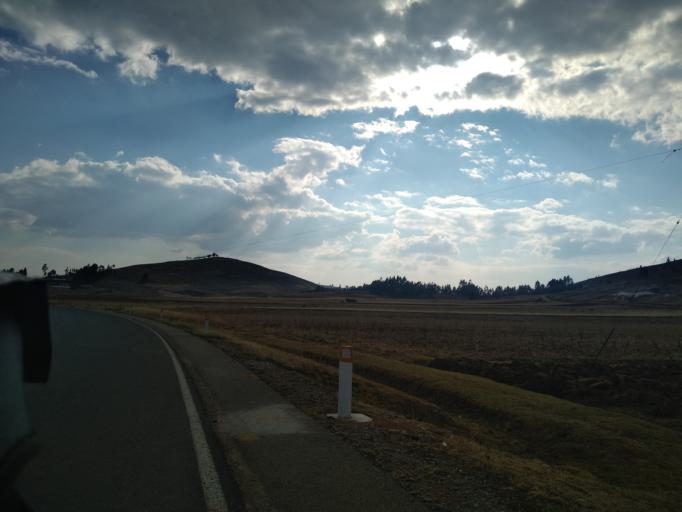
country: PE
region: Cajamarca
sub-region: Provincia de Cajamarca
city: Encanada
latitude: -7.1385
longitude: -78.3867
